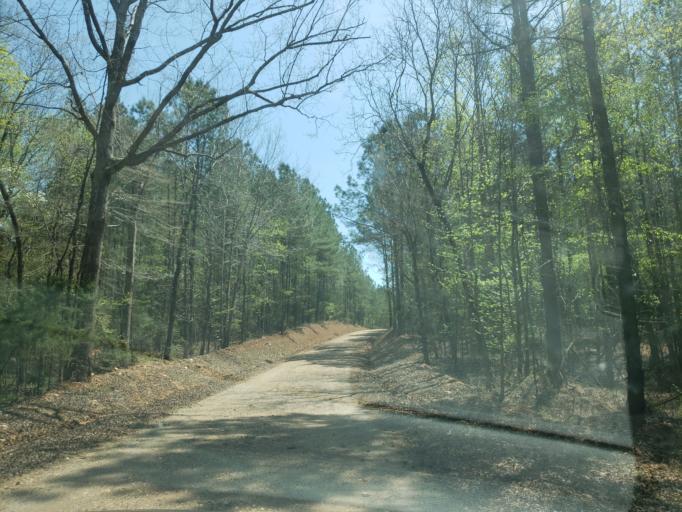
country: US
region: Alabama
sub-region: Tallapoosa County
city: Camp Hill
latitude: 32.6546
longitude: -85.6588
